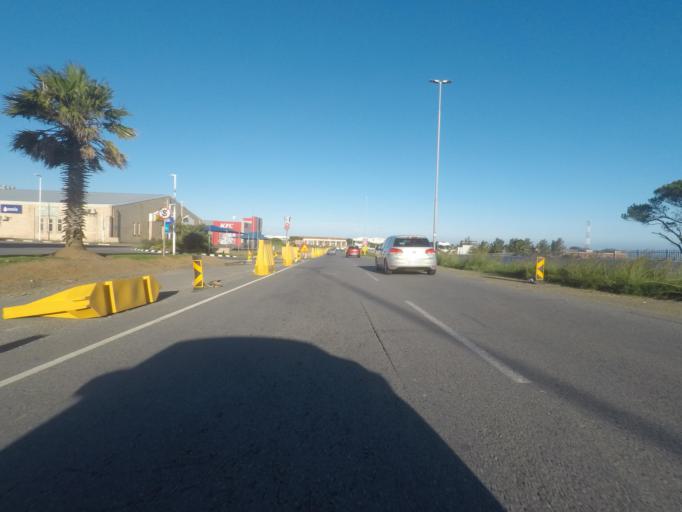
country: ZA
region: Eastern Cape
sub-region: Buffalo City Metropolitan Municipality
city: East London
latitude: -33.0356
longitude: 27.8670
